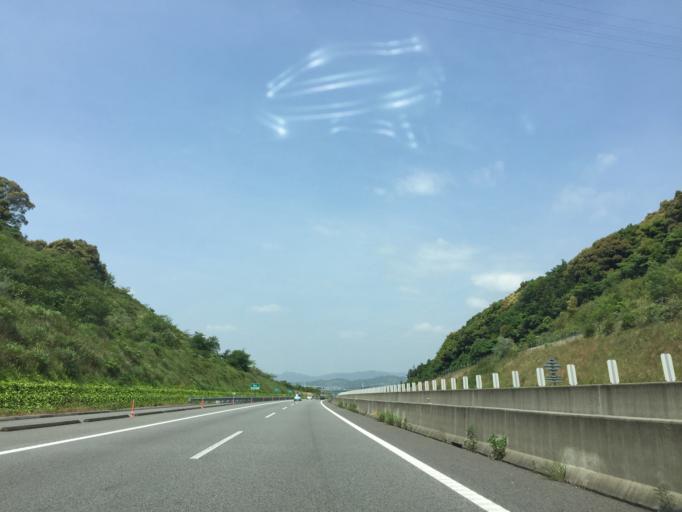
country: JP
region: Shizuoka
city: Hamakita
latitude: 34.8258
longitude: 137.8532
